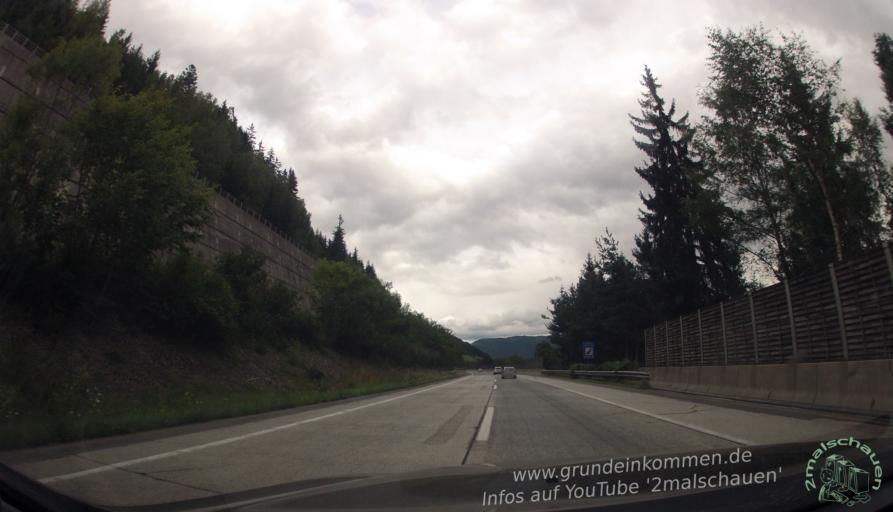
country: AT
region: Salzburg
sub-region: Politischer Bezirk Sankt Johann im Pongau
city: Huttau
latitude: 47.4315
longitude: 13.2796
